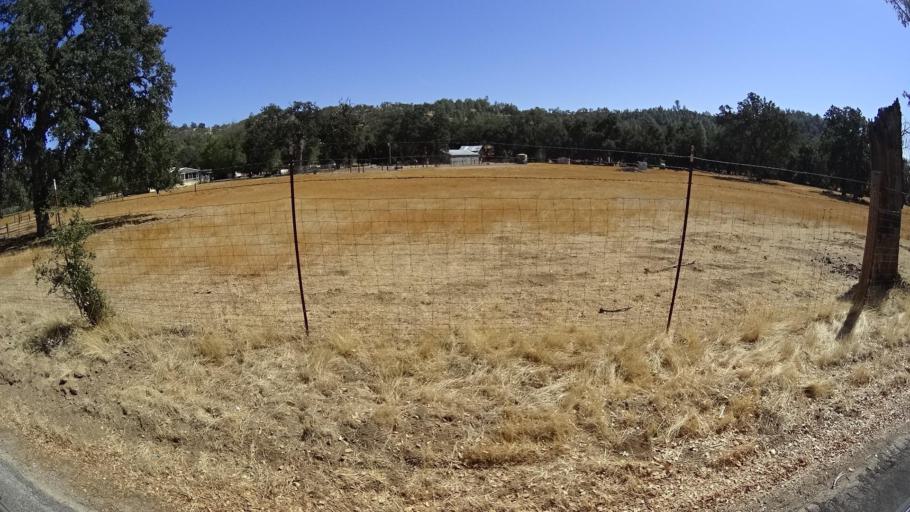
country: US
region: California
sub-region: San Luis Obispo County
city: Lake Nacimiento
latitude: 35.8134
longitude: -121.0805
